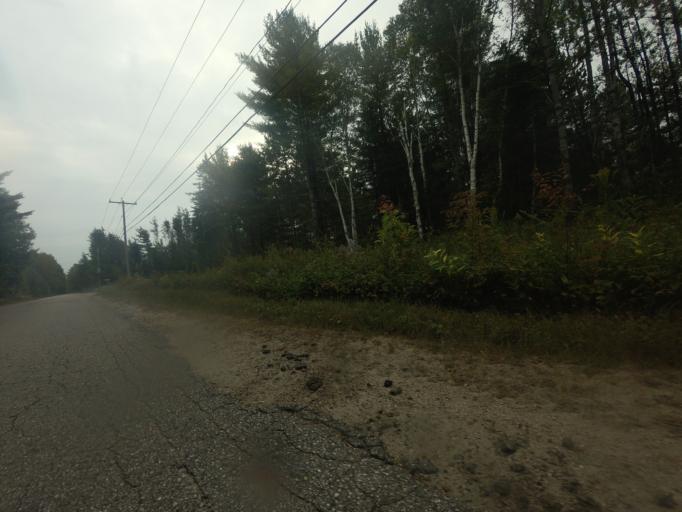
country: CA
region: Quebec
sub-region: Outaouais
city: Maniwaki
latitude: 46.0845
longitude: -76.0157
